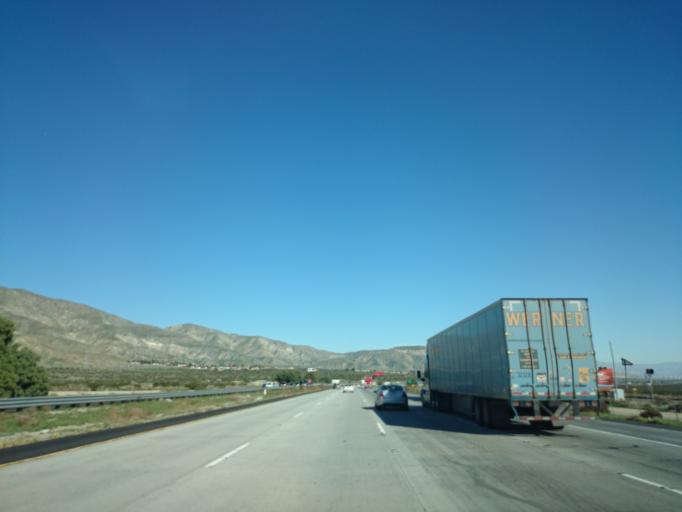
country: US
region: California
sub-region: Riverside County
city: Cabazon
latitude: 33.9227
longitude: -116.7431
